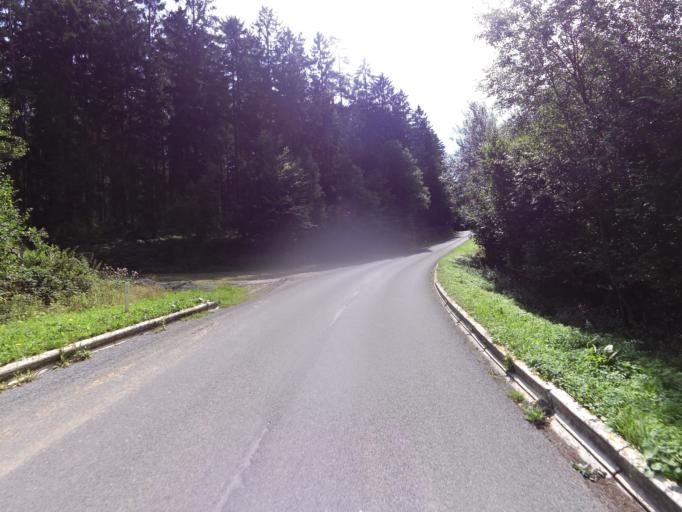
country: BE
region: Wallonia
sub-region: Province du Luxembourg
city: Saint-Hubert
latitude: 50.0410
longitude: 5.3562
